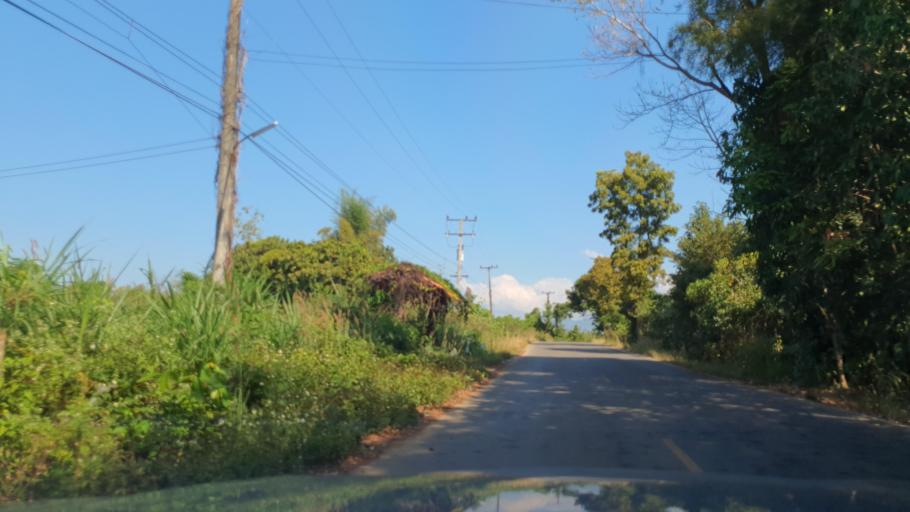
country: TH
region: Nan
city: Pua
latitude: 19.1513
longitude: 100.9101
